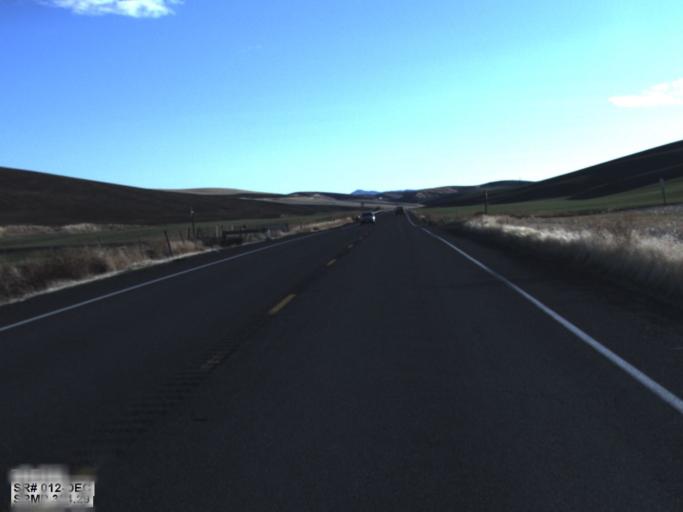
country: US
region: Washington
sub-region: Walla Walla County
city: Waitsburg
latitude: 46.2245
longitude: -118.1376
